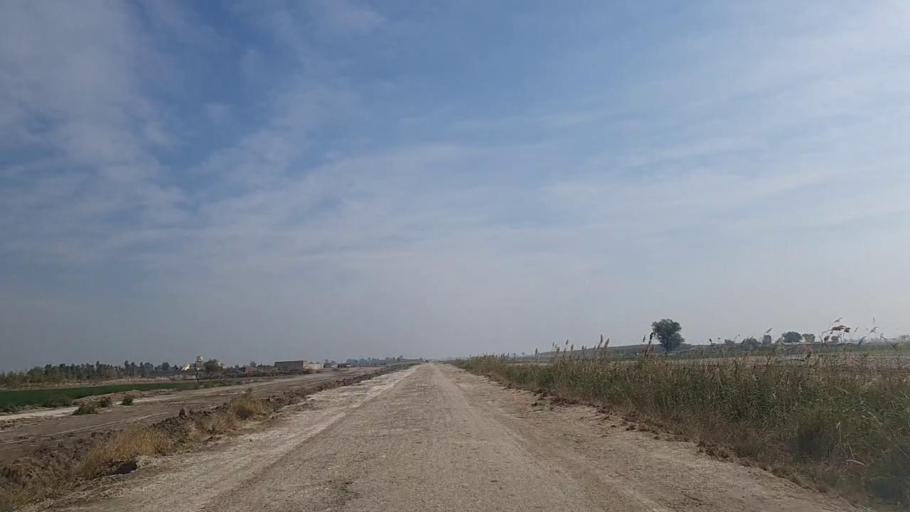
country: PK
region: Sindh
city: Nawabshah
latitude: 26.3319
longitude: 68.4517
